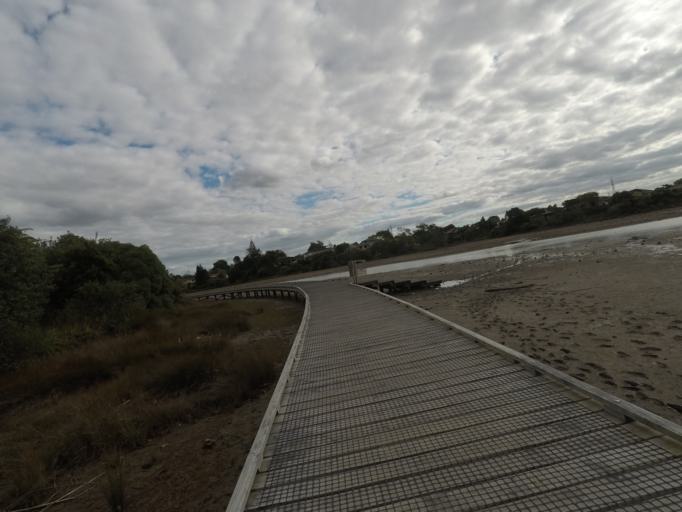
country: NZ
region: Auckland
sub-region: Auckland
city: Papakura
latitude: -37.0629
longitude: 174.9333
